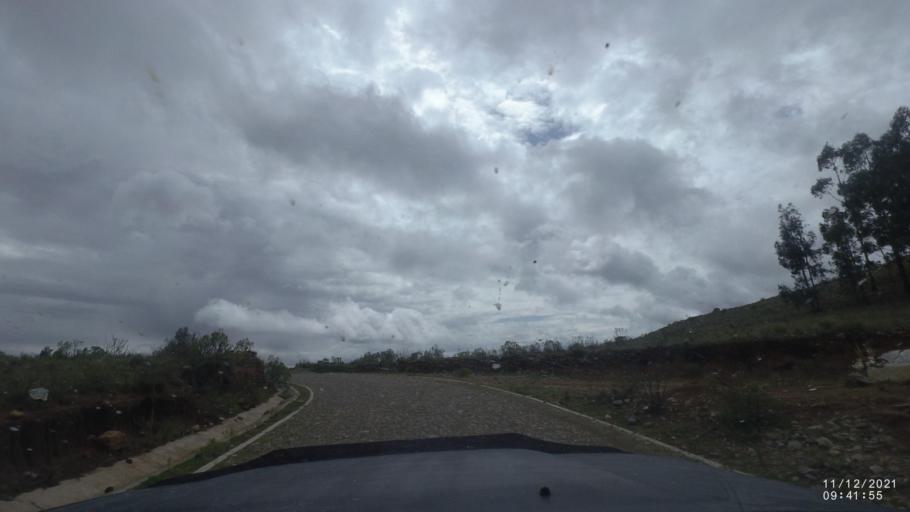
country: BO
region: Cochabamba
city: Tarata
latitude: -17.8128
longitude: -65.9759
